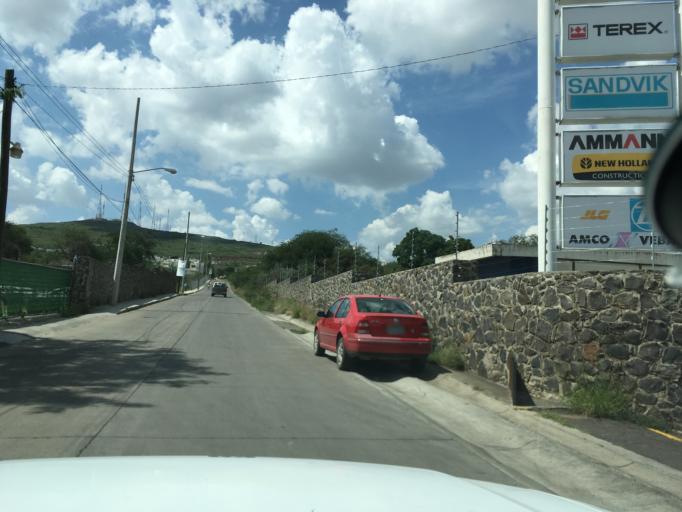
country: MX
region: Jalisco
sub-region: Tlajomulco de Zuniga
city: Altus Bosques
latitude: 20.5802
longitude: -103.3664
